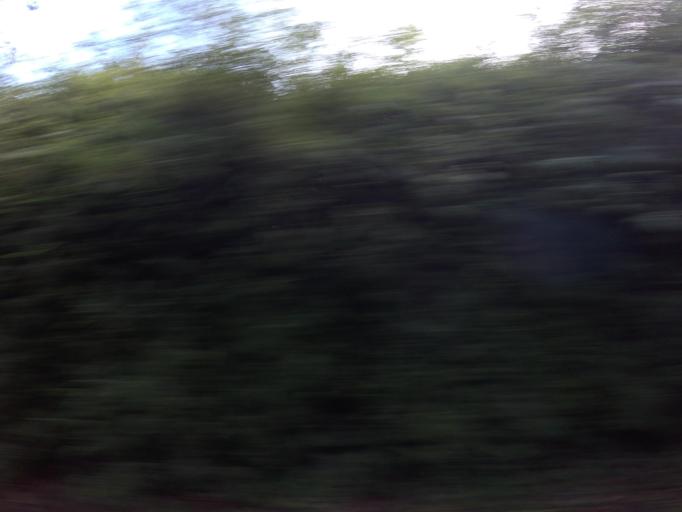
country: CO
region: Cundinamarca
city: Zipacon
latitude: 4.7646
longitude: -74.4430
